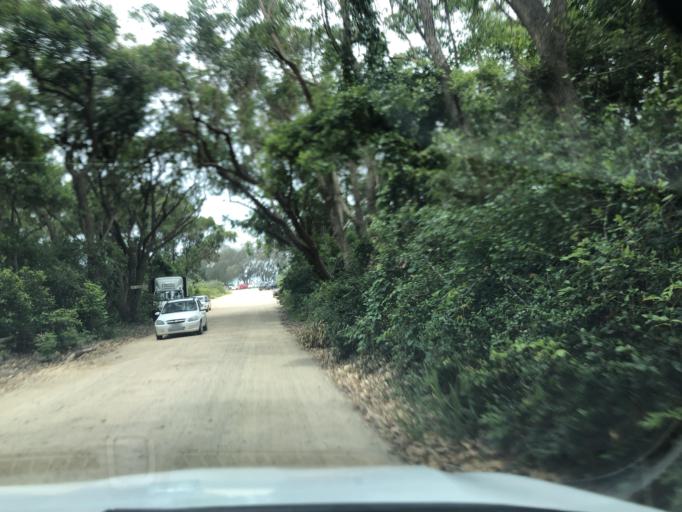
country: BR
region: Santa Catarina
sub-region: Florianopolis
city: Lagoa
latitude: -27.5232
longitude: -48.4189
